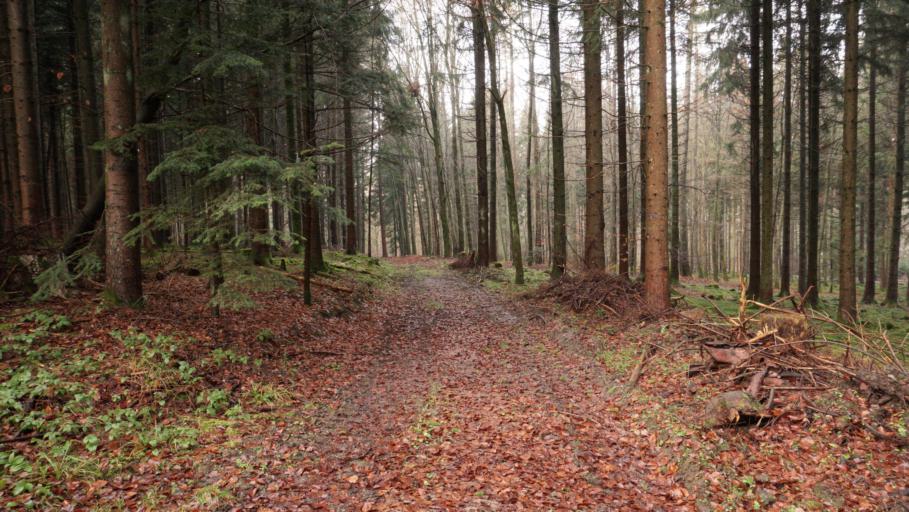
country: DE
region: Baden-Wuerttemberg
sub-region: Karlsruhe Region
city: Reichartshausen
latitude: 49.4019
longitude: 8.9550
